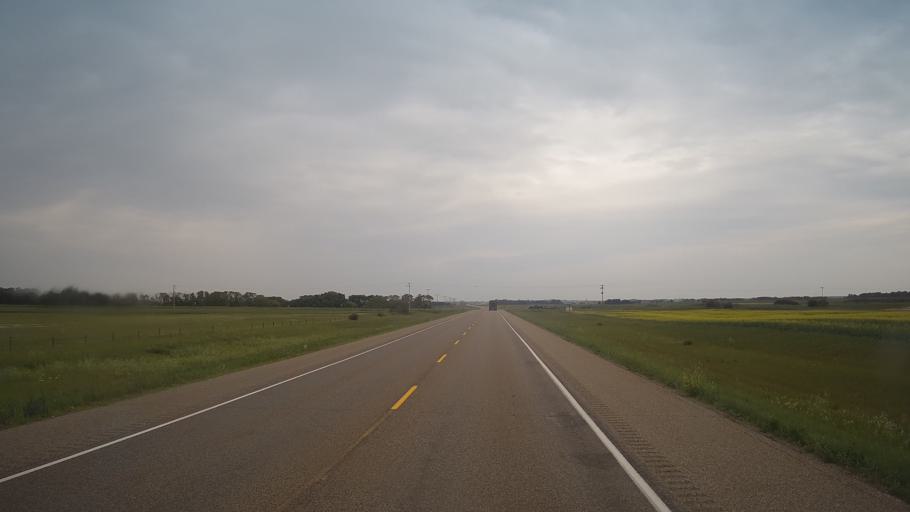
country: CA
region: Saskatchewan
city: Langham
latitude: 52.1294
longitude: -107.0937
